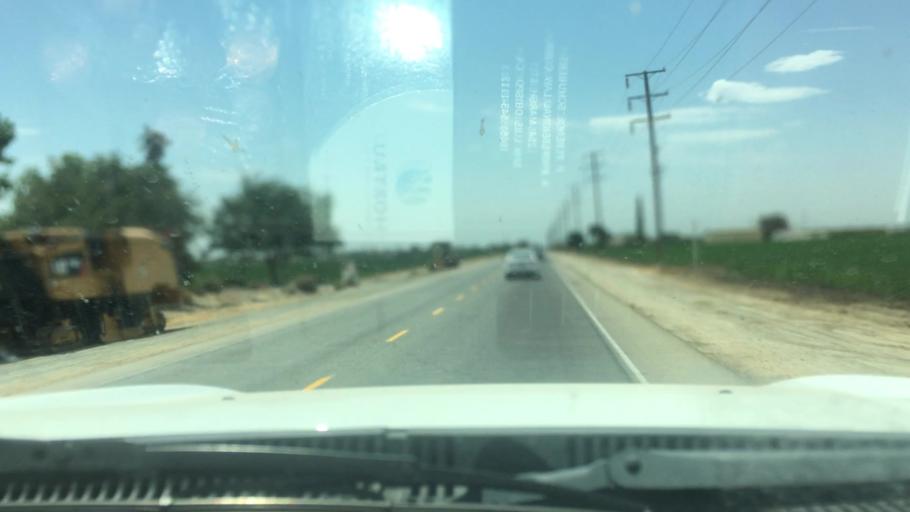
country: US
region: California
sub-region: Tulare County
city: Tipton
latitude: 36.0657
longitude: -119.2919
